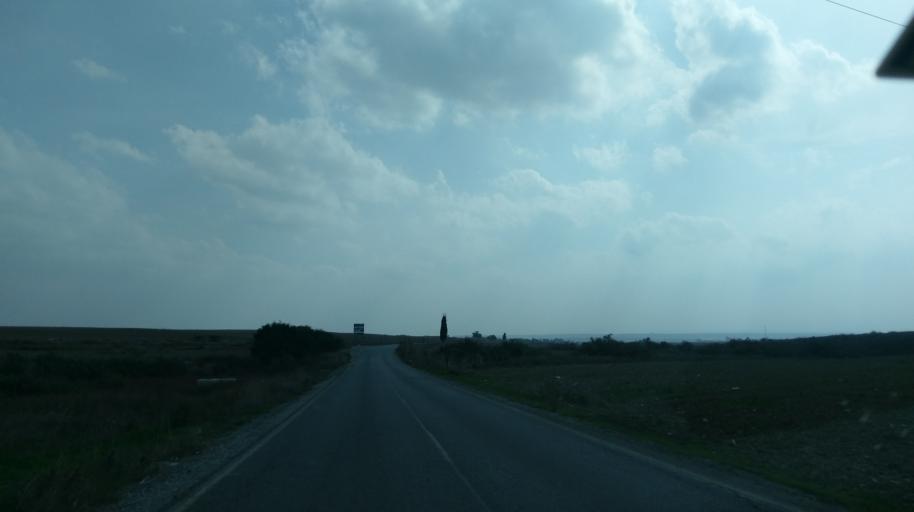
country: CY
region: Lefkosia
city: Mammari
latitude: 35.2480
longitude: 33.1517
